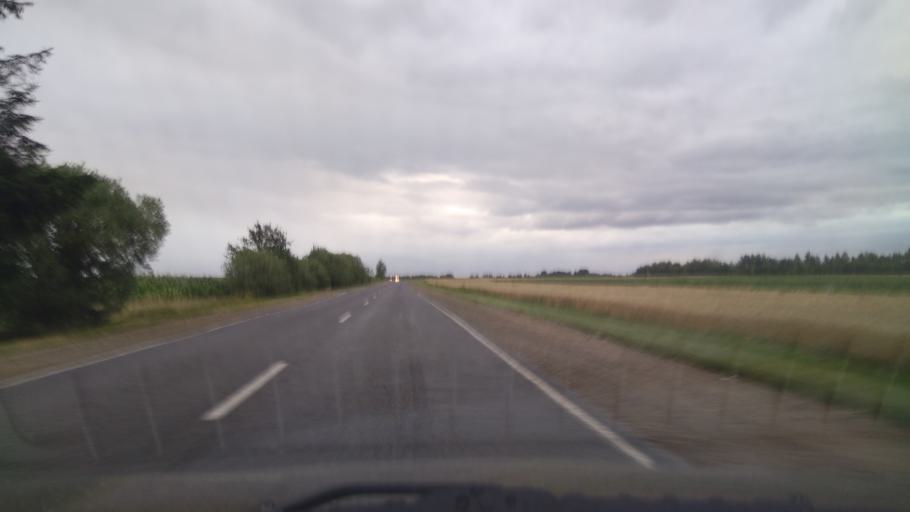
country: BY
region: Brest
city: Byaroza
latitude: 52.4273
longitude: 24.9808
